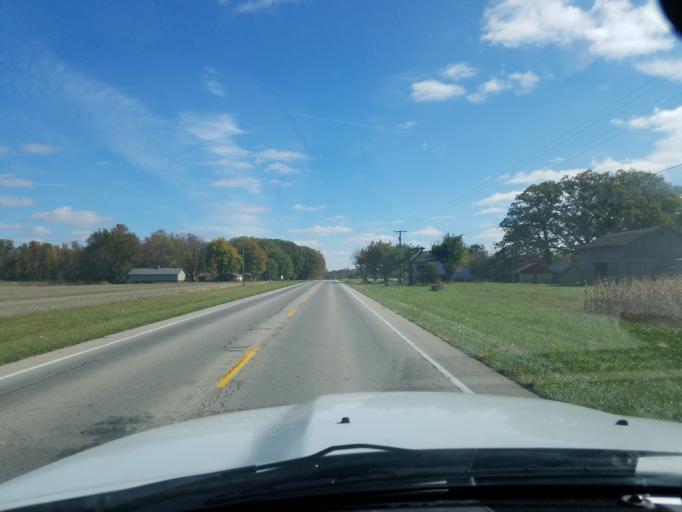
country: US
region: Indiana
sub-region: Ripley County
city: Versailles
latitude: 39.0747
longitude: -85.2826
